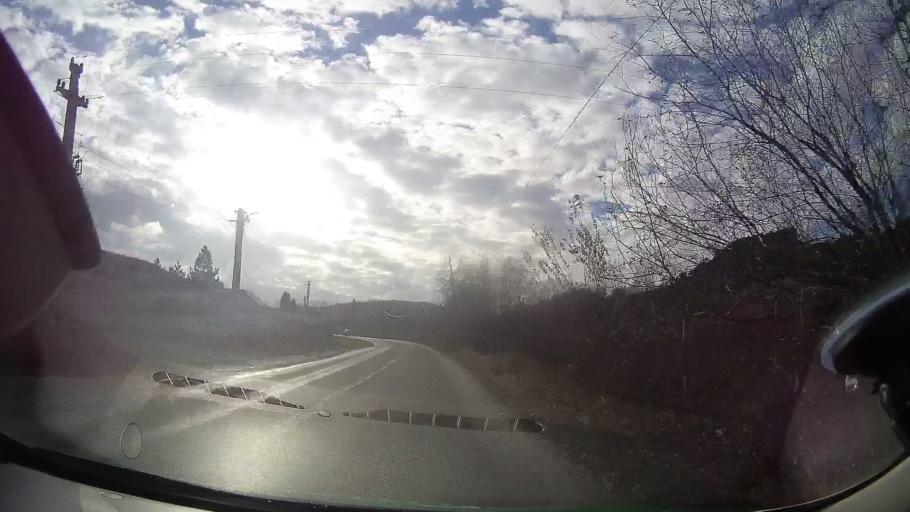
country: RO
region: Cluj
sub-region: Comuna Savadisla
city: Savadisla
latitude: 46.6795
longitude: 23.4561
